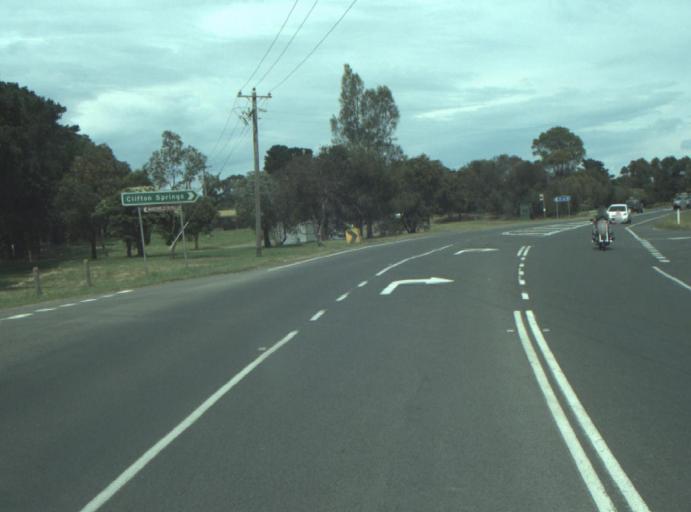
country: AU
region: Victoria
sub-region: Greater Geelong
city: Clifton Springs
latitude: -38.1597
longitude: 144.5841
